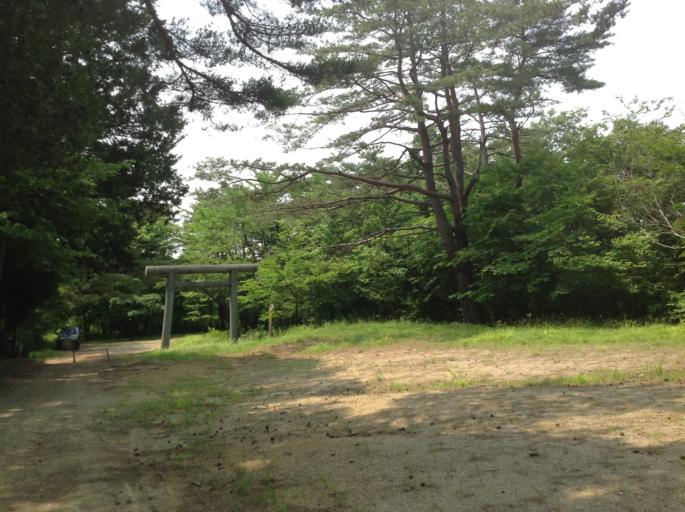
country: JP
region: Iwate
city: Ichinoseki
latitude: 38.9418
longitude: 141.1227
